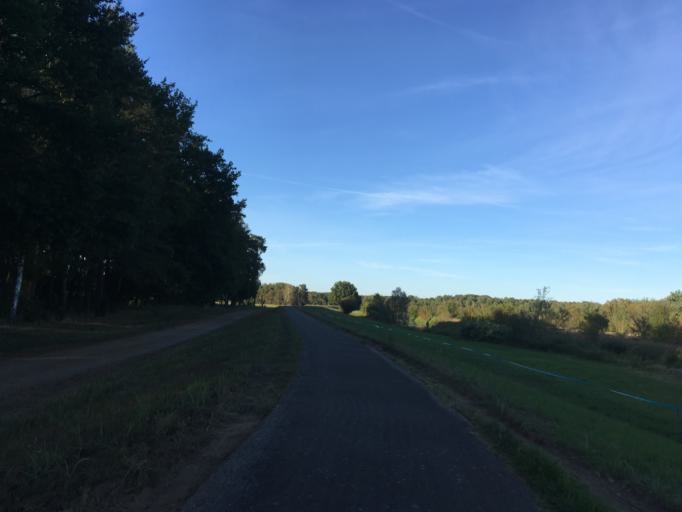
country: PL
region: Lubusz
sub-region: Powiat zarski
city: Trzebiel
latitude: 51.6559
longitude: 14.7543
